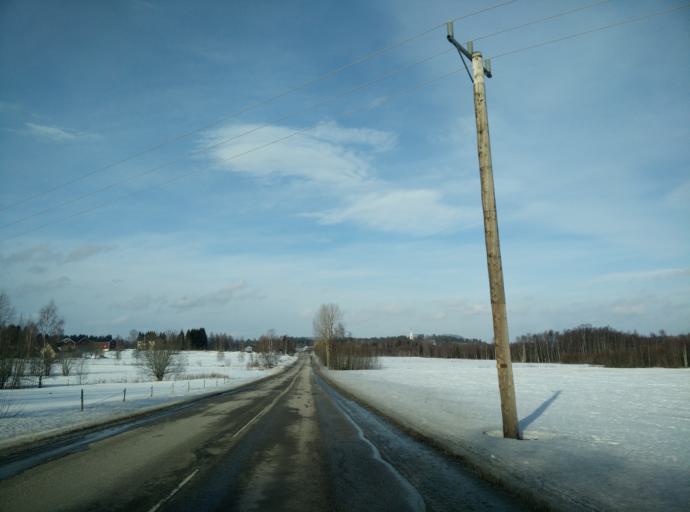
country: SE
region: Vaesternorrland
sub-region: Sundsvalls Kommun
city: Njurundabommen
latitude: 62.2403
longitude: 17.3813
